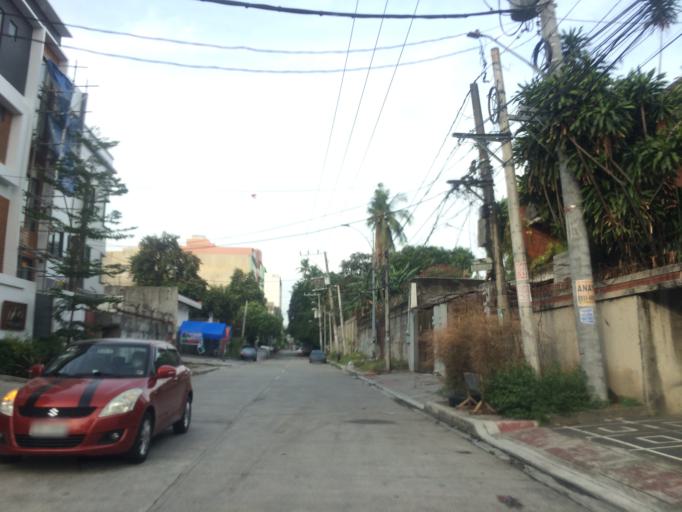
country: PH
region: Calabarzon
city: Del Monte
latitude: 14.6248
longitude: 121.0062
